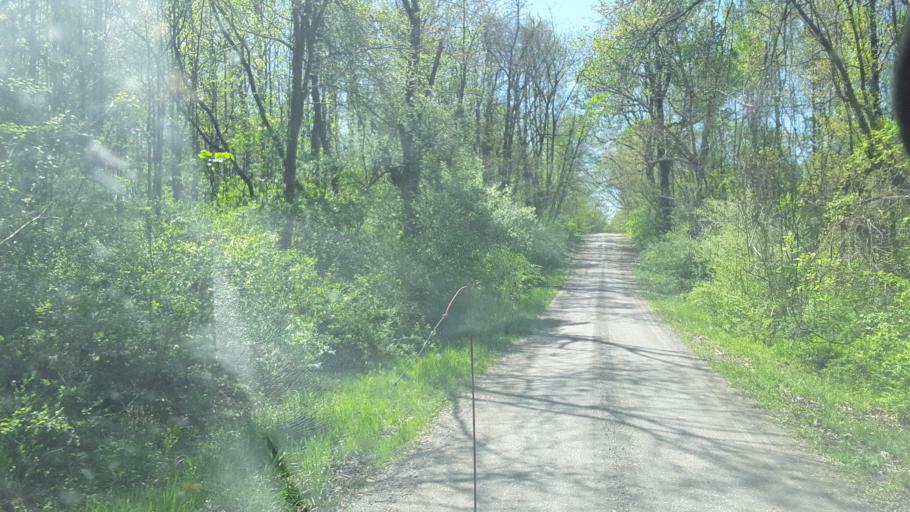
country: US
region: Ohio
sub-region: Noble County
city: Caldwell
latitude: 39.7710
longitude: -81.6166
